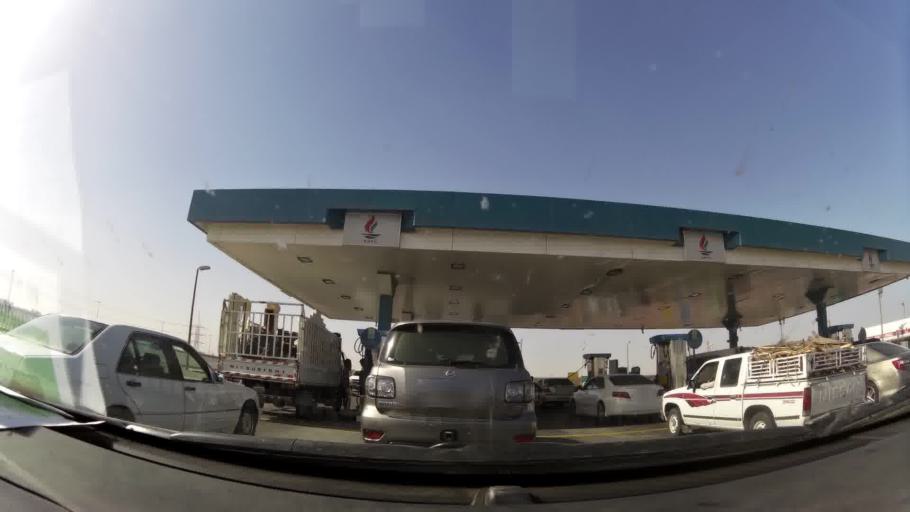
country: KW
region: Al Asimah
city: Ar Rabiyah
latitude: 29.2762
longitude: 47.8101
